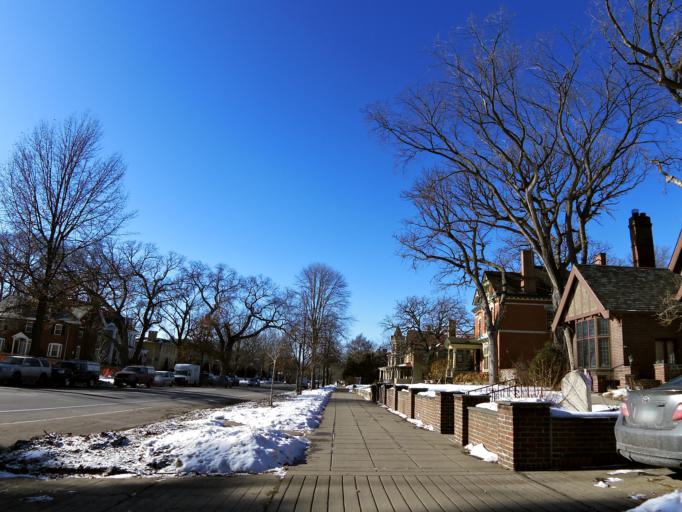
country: US
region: Minnesota
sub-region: Ramsey County
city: Saint Paul
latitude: 44.9415
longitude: -93.1203
